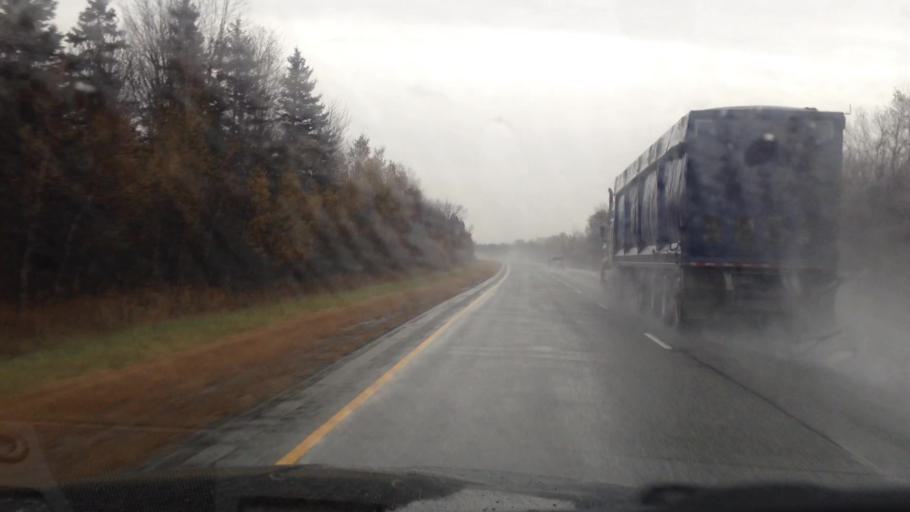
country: CA
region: Ontario
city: Casselman
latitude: 45.3150
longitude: -75.1881
